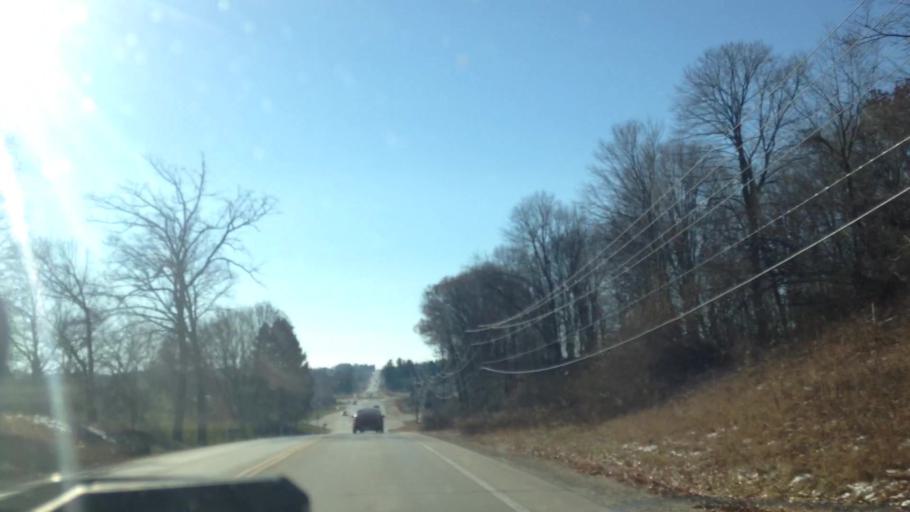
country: US
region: Wisconsin
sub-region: Washington County
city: West Bend
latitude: 43.4022
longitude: -88.1612
